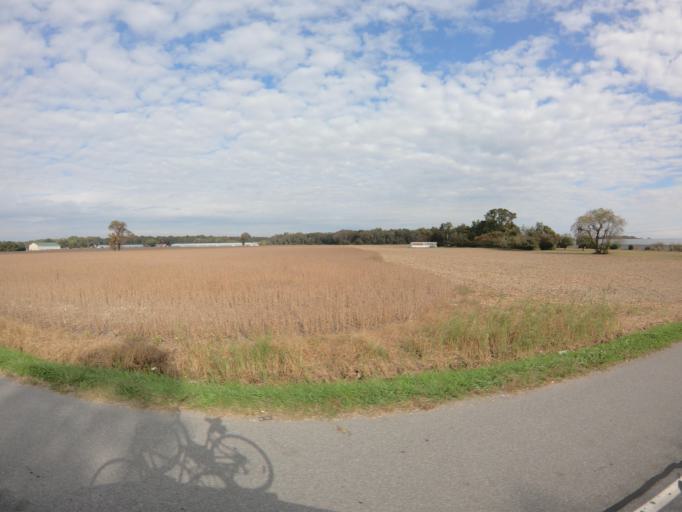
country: US
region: Delaware
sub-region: Sussex County
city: Bridgeville
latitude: 38.7080
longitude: -75.5453
